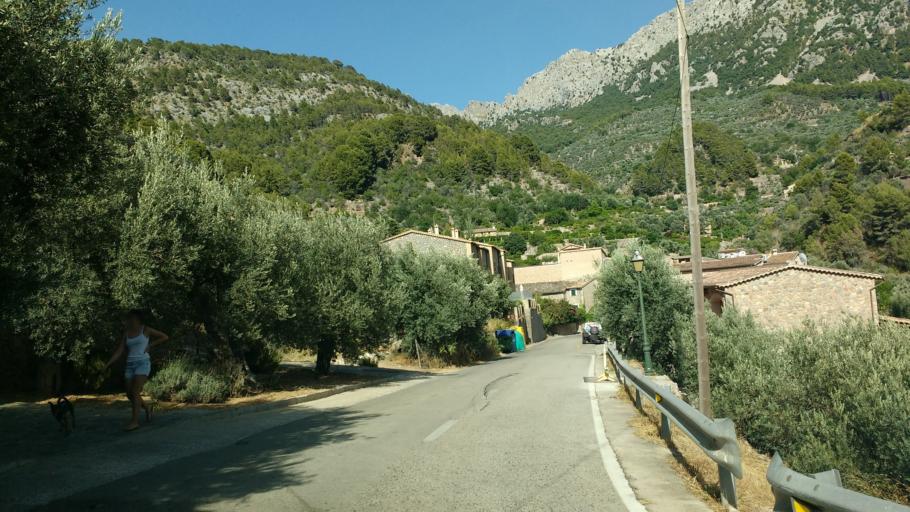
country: ES
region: Balearic Islands
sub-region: Illes Balears
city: Fornalutx
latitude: 39.7851
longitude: 2.7437
